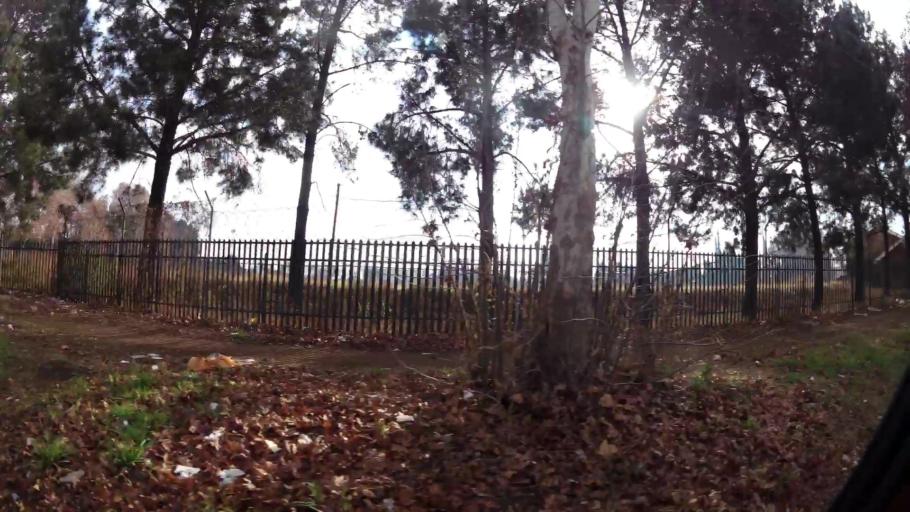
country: ZA
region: Gauteng
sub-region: Sedibeng District Municipality
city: Vanderbijlpark
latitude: -26.7027
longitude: 27.8174
